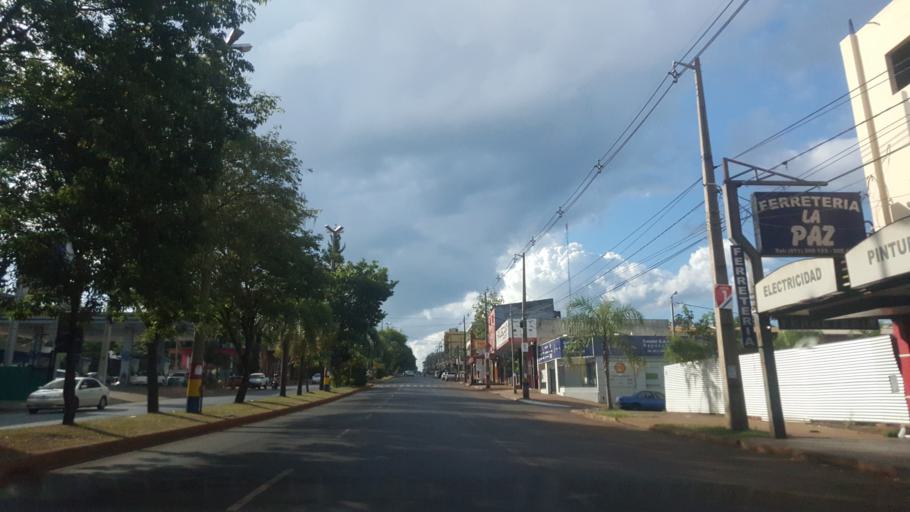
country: PY
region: Itapua
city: Encarnacion
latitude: -27.3345
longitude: -55.8585
